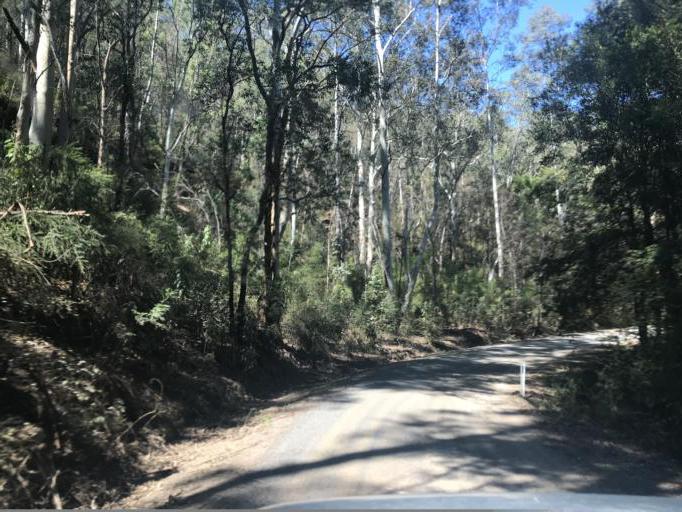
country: AU
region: New South Wales
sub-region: Wyong Shire
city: Little Jilliby
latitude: -33.1676
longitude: 151.0687
